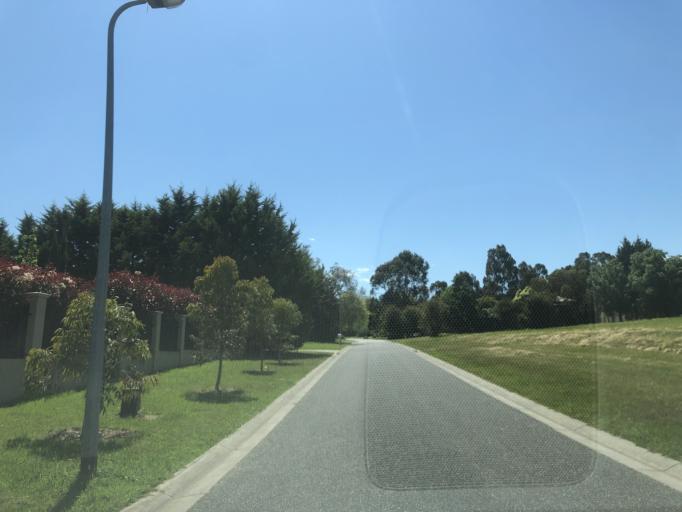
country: AU
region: Victoria
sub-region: Casey
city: Endeavour Hills
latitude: -37.9846
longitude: 145.2808
